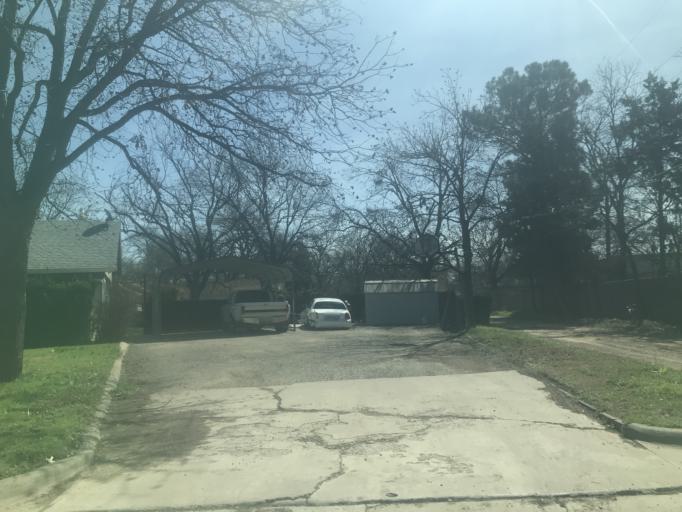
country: US
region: Texas
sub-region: Taylor County
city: Abilene
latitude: 32.4404
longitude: -99.7753
